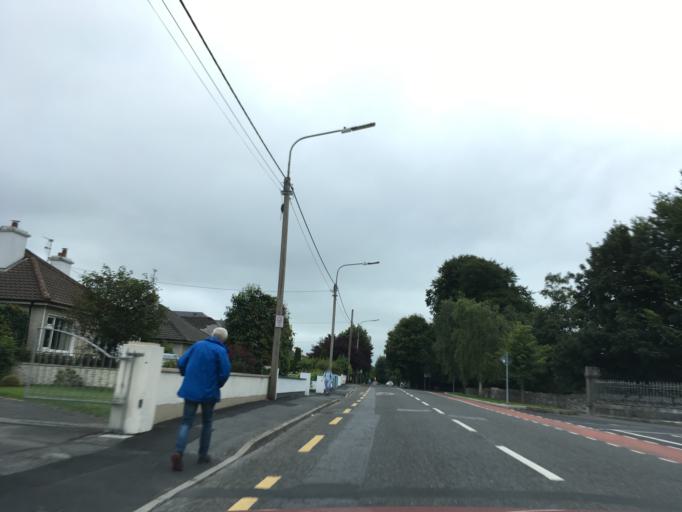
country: IE
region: Munster
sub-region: An Clar
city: Ennis
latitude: 52.8325
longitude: -8.9820
